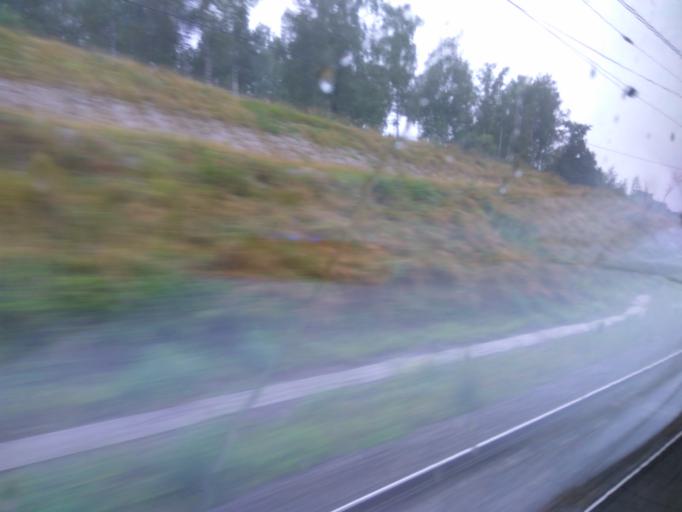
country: RU
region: Moskovskaya
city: Ozherel'ye
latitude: 54.8167
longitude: 38.2681
